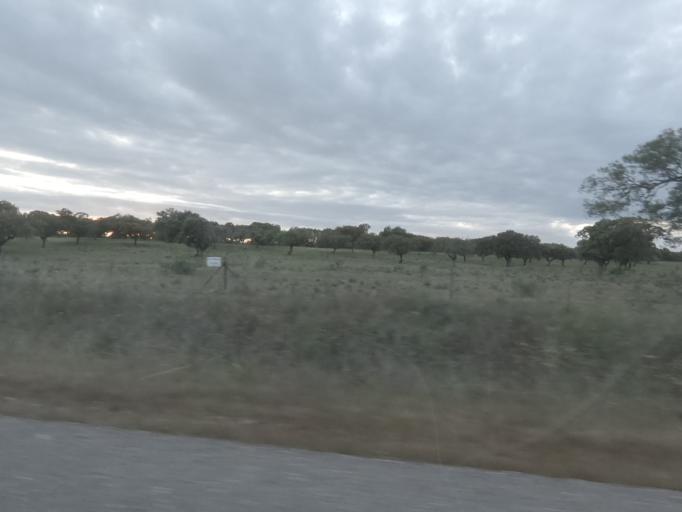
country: ES
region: Extremadura
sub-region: Provincia de Badajoz
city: La Roca de la Sierra
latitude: 39.0735
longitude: -6.7523
